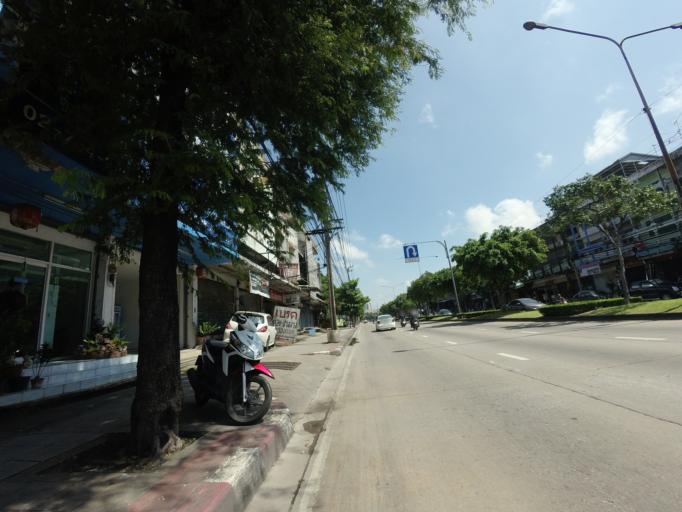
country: TH
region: Bangkok
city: Bueng Kum
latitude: 13.7884
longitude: 100.6504
